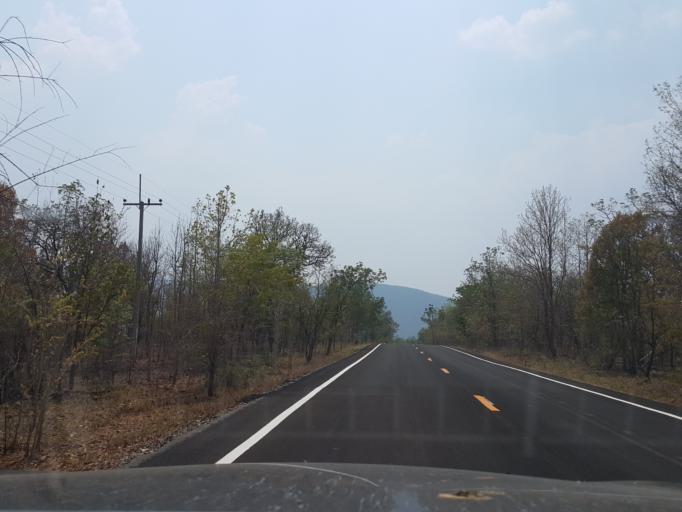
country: TH
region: Lampang
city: Mae Phrik
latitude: 17.4887
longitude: 99.0974
